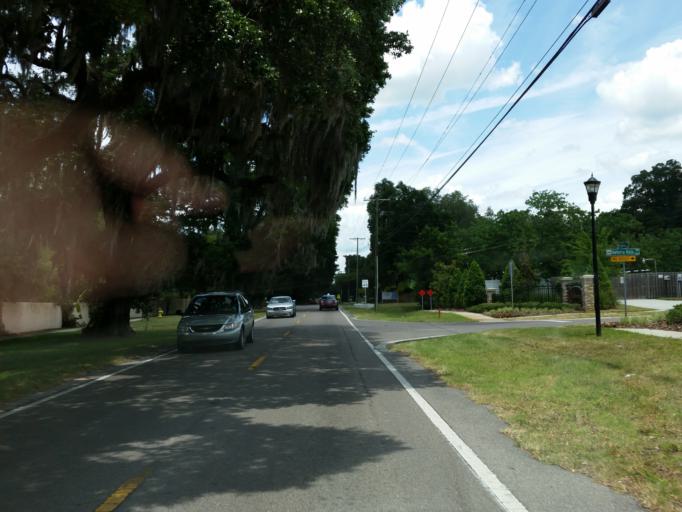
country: US
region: Florida
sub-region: Hillsborough County
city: Valrico
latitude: 27.9591
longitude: -82.2528
